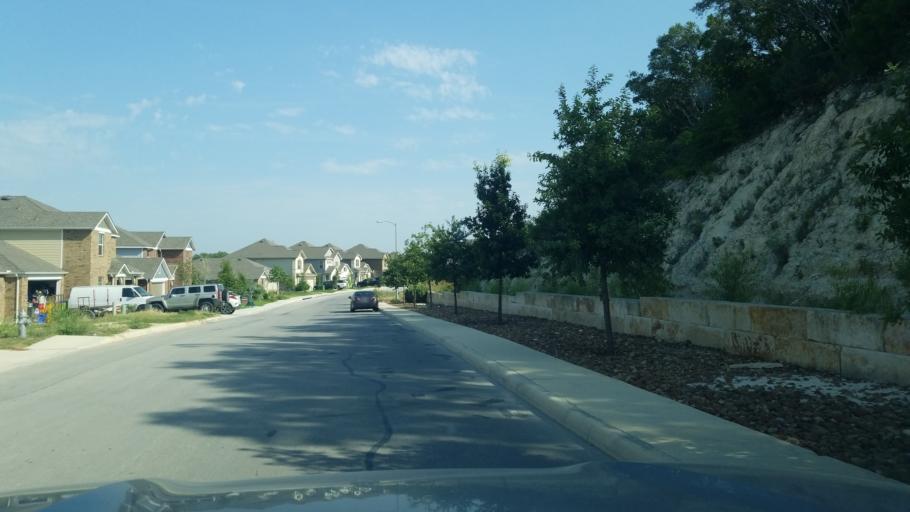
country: US
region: Texas
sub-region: Medina County
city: La Coste
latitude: 29.4036
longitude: -98.7863
